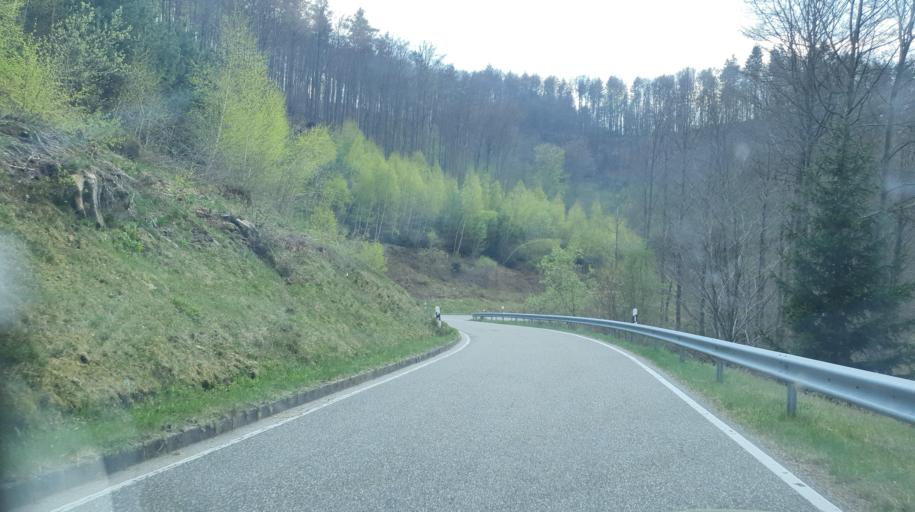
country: DE
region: Rheinland-Pfalz
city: Leimen
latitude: 49.2826
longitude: 7.7456
